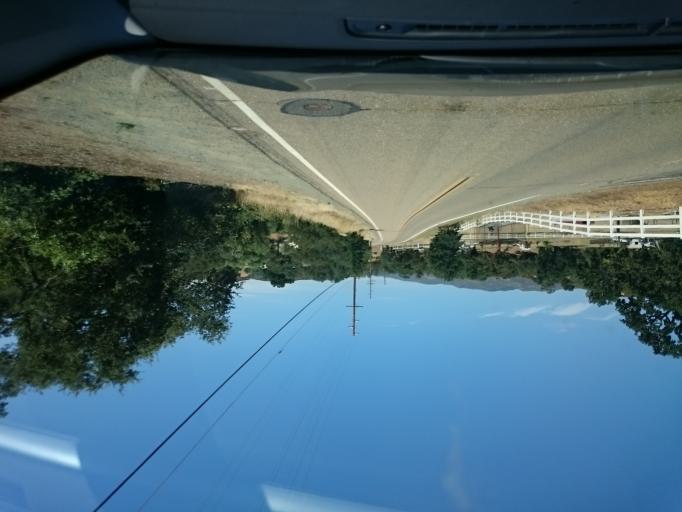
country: US
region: California
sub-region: Calaveras County
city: Rancho Calaveras
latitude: 38.1523
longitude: -120.8334
